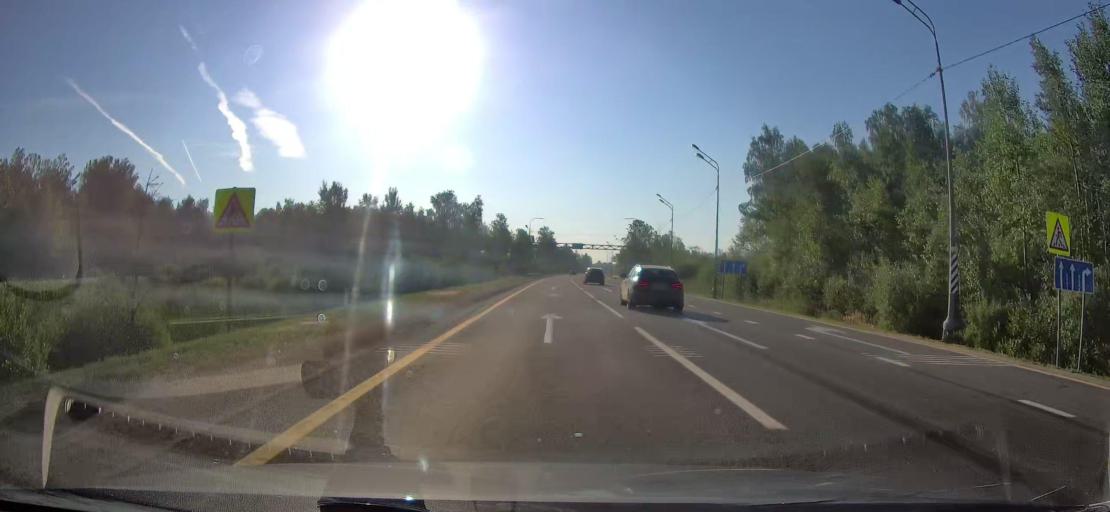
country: RU
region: Leningrad
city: Sinyavino
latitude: 59.9082
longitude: 31.0424
